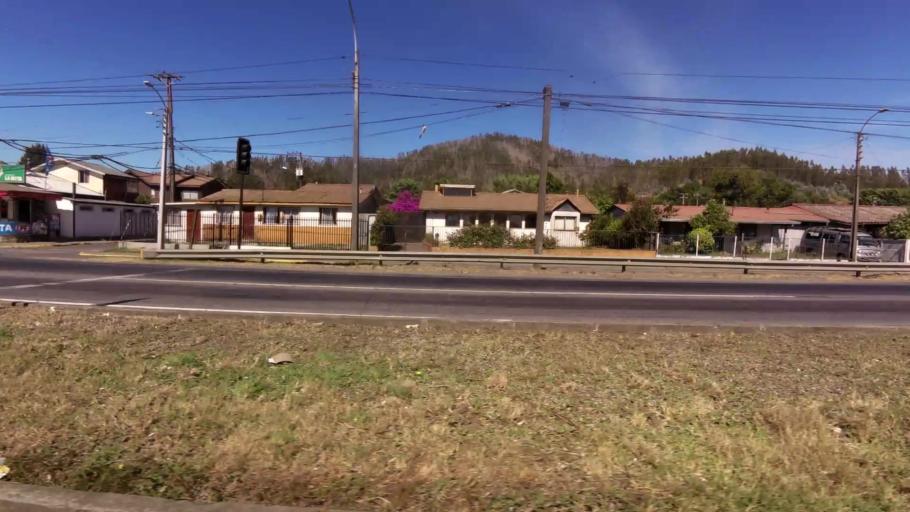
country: CL
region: Biobio
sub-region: Provincia de Concepcion
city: Concepcion
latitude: -36.7921
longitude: -73.0253
